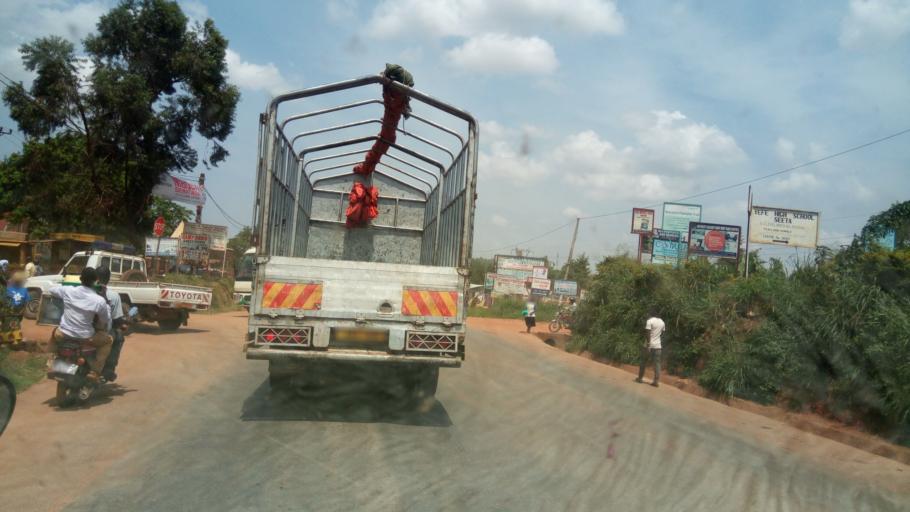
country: UG
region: Central Region
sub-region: Wakiso District
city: Bweyogerere
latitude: 0.3644
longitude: 32.7005
